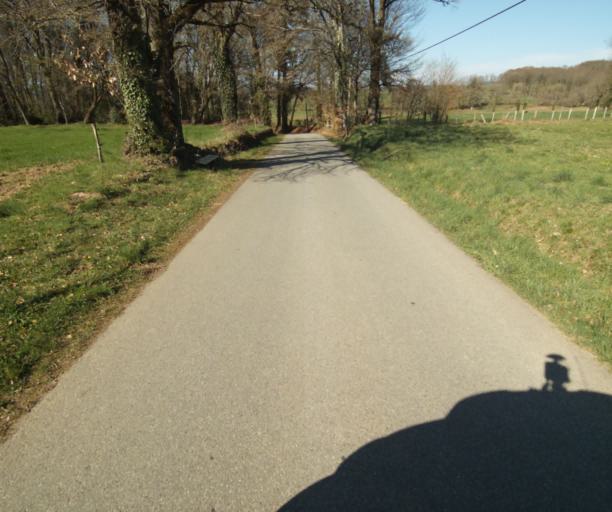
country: FR
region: Limousin
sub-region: Departement de la Correze
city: Chamboulive
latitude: 45.4734
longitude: 1.7361
